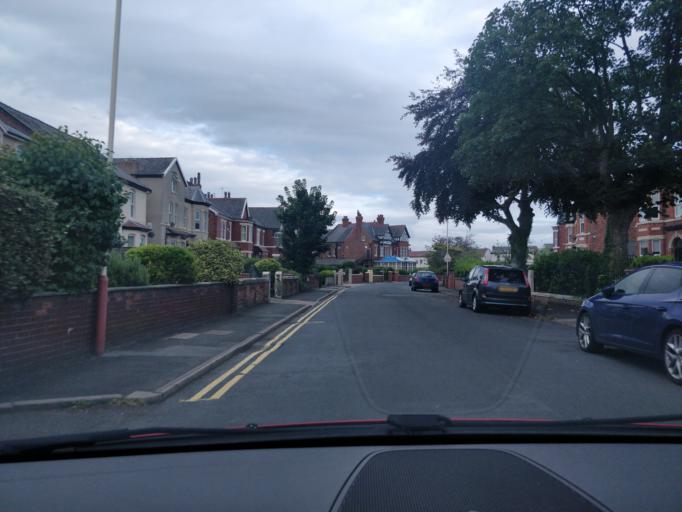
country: GB
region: England
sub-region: Sefton
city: Southport
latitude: 53.6511
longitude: -2.9899
